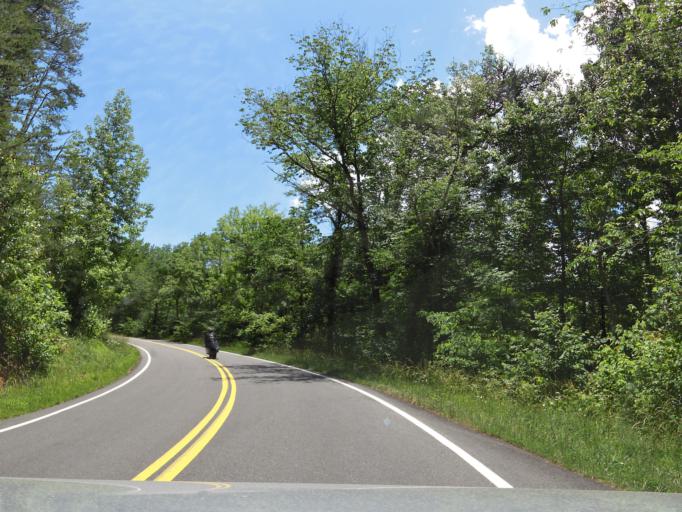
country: US
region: Tennessee
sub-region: Loudon County
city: Greenback
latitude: 35.5105
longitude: -83.9867
